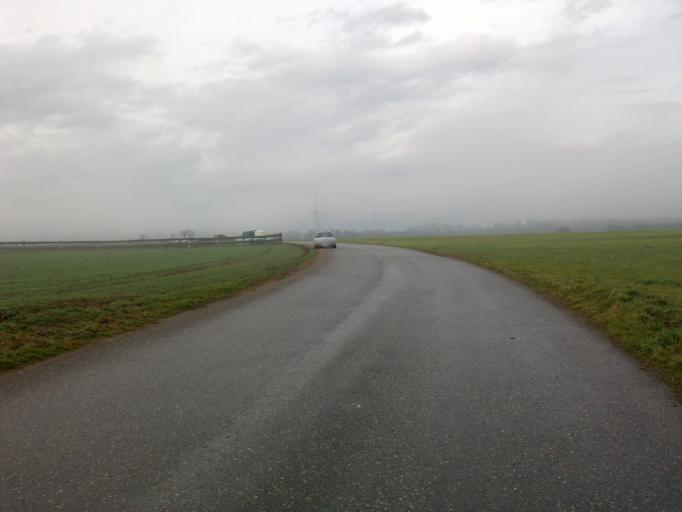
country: AT
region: Styria
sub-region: Politischer Bezirk Murtal
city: Weisskirchen in Steiermark
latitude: 47.1663
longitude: 14.7411
